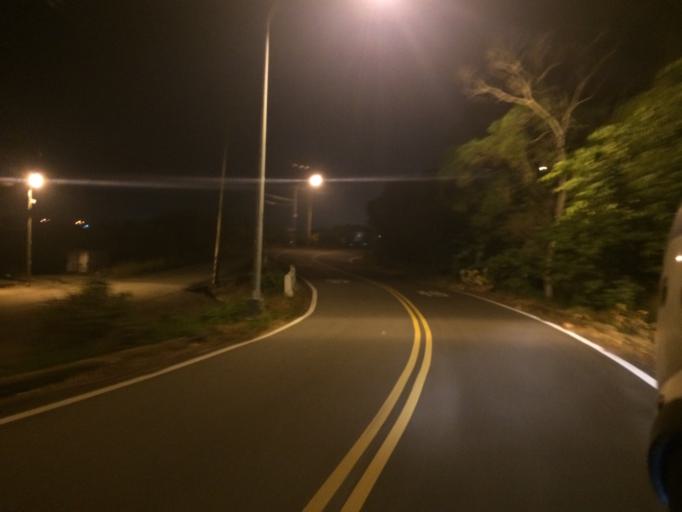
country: TW
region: Taiwan
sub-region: Hsinchu
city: Hsinchu
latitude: 24.7338
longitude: 120.9063
